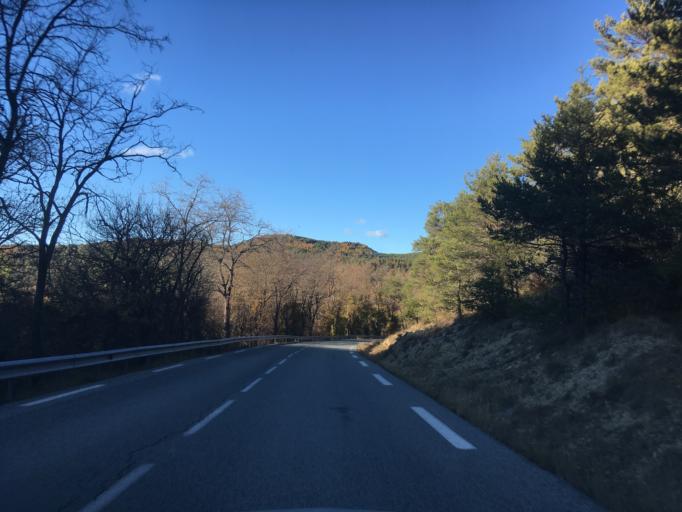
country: FR
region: Provence-Alpes-Cote d'Azur
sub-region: Departement des Alpes-de-Haute-Provence
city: Castellane
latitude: 43.7386
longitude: 6.4994
